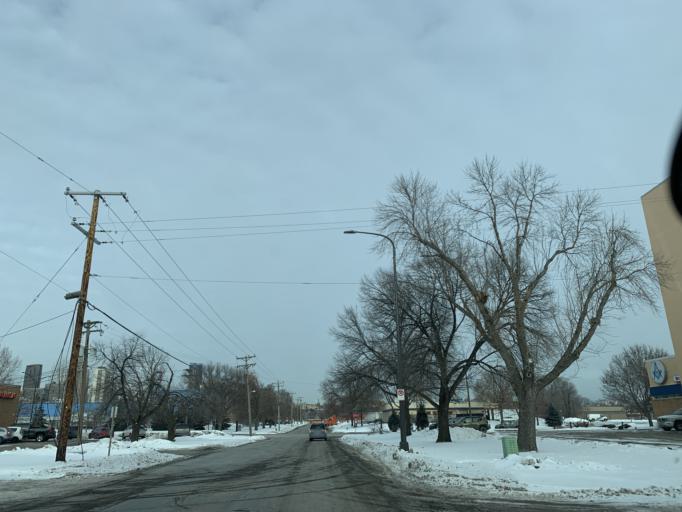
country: US
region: Minnesota
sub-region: Ramsey County
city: Saint Paul
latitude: 44.9382
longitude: -93.0799
